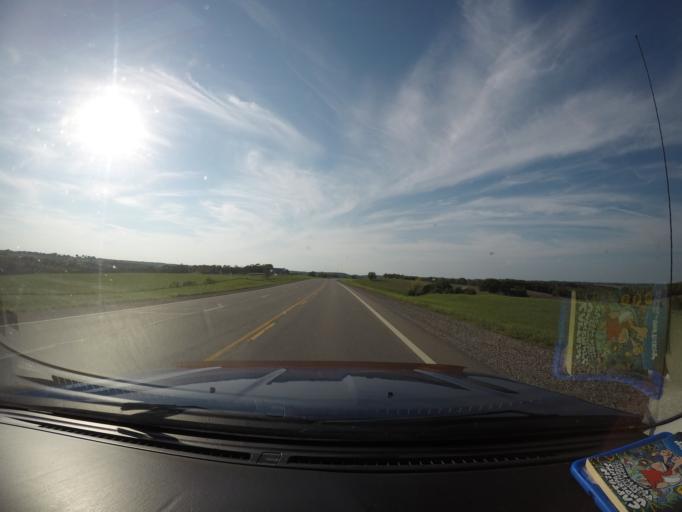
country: US
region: Kansas
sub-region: Atchison County
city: Atchison
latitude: 39.4718
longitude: -95.0984
